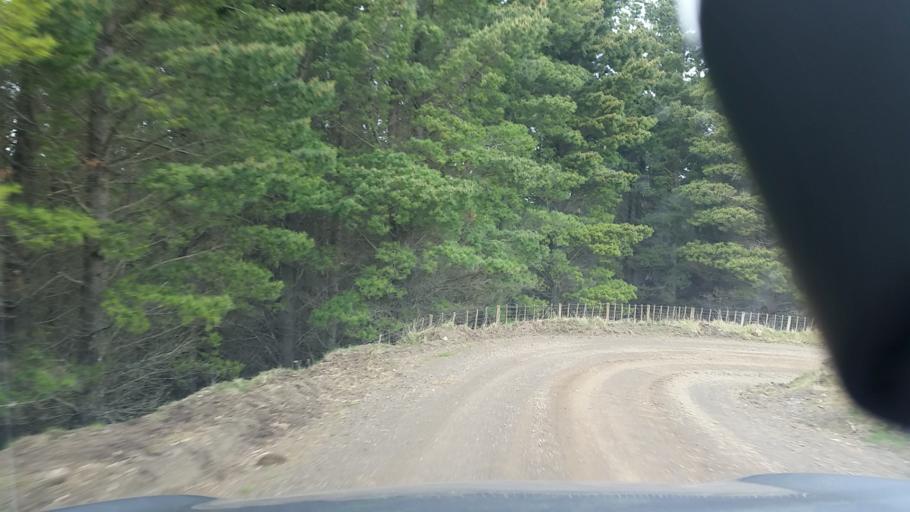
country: NZ
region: Hawke's Bay
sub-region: Napier City
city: Napier
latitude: -39.2182
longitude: 176.9792
